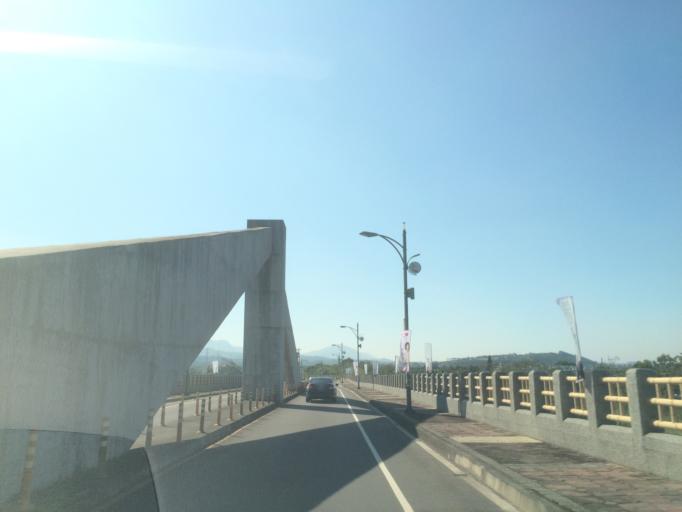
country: TW
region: Taiwan
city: Lugu
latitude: 23.7891
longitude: 120.7058
